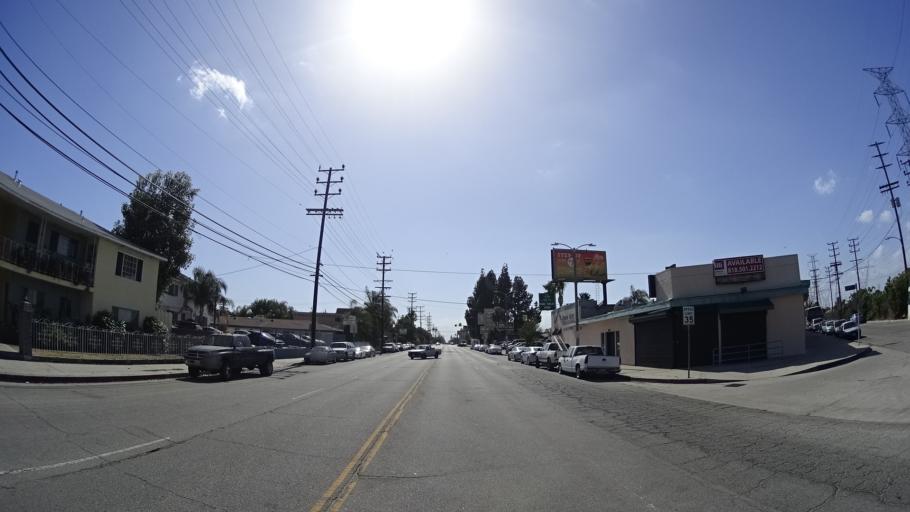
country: US
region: California
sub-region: Los Angeles County
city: North Hollywood
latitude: 34.1794
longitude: -118.3665
